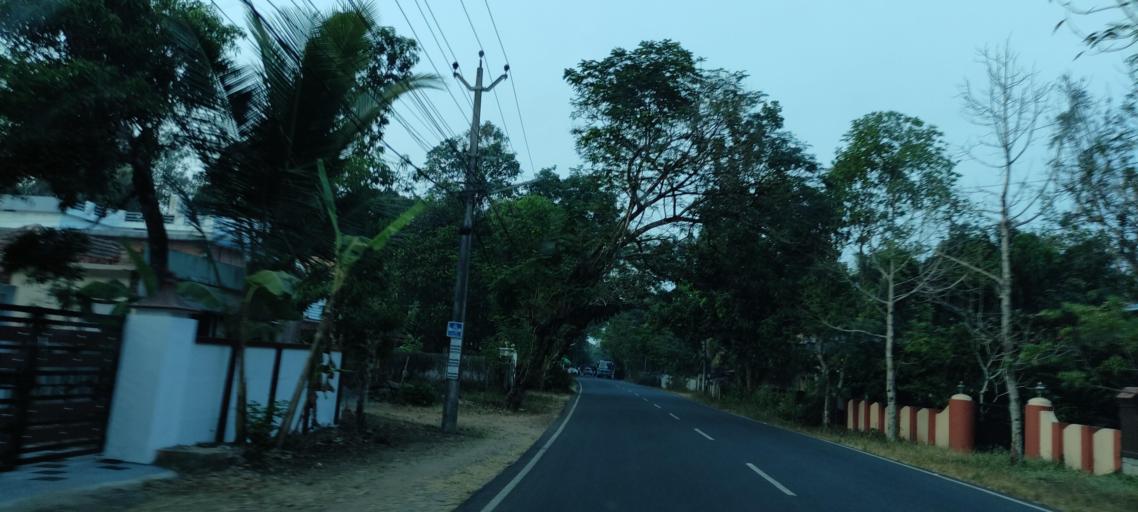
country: IN
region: Kerala
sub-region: Alappuzha
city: Mavelikara
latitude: 9.2935
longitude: 76.5330
